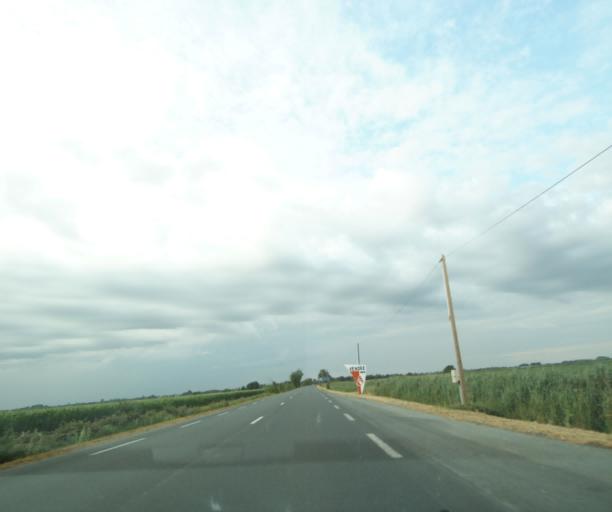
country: FR
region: Poitou-Charentes
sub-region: Departement de la Charente-Maritime
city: Marans
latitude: 46.3515
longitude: -0.9949
